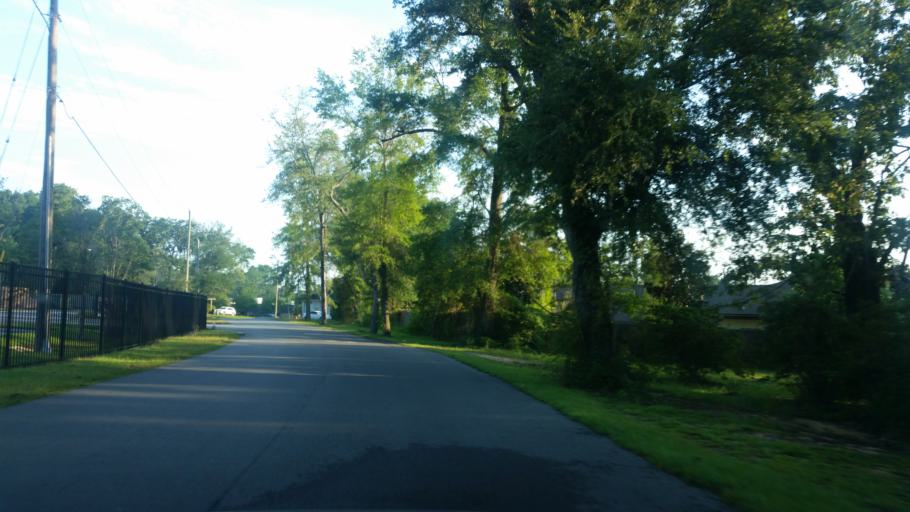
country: US
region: Florida
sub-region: Escambia County
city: Ferry Pass
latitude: 30.5387
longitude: -87.2160
